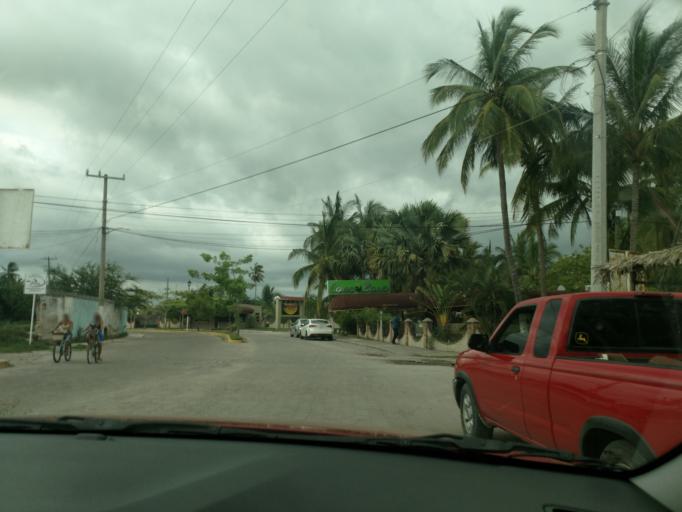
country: MX
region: Nayarit
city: San Blas
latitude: 21.5323
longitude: -105.2837
